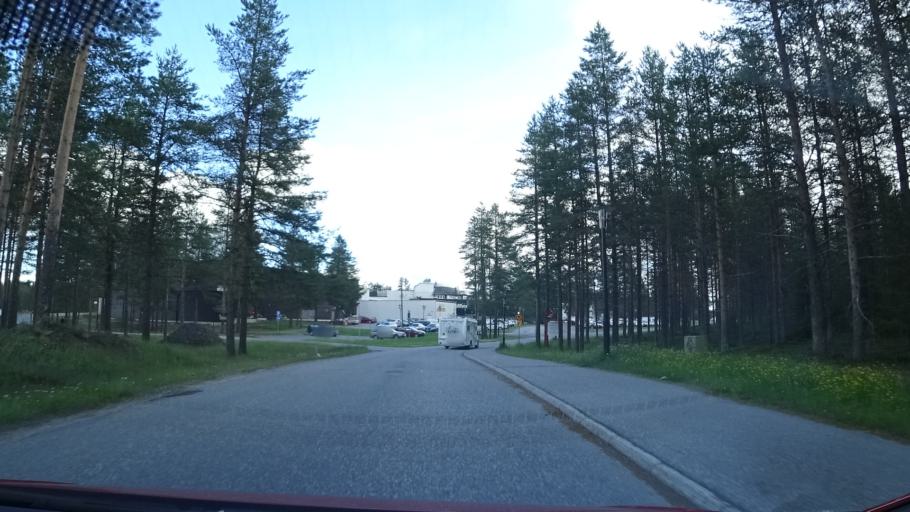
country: FI
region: Northern Ostrobothnia
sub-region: Koillismaa
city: Kuusamo
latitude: 66.0006
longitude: 29.1632
